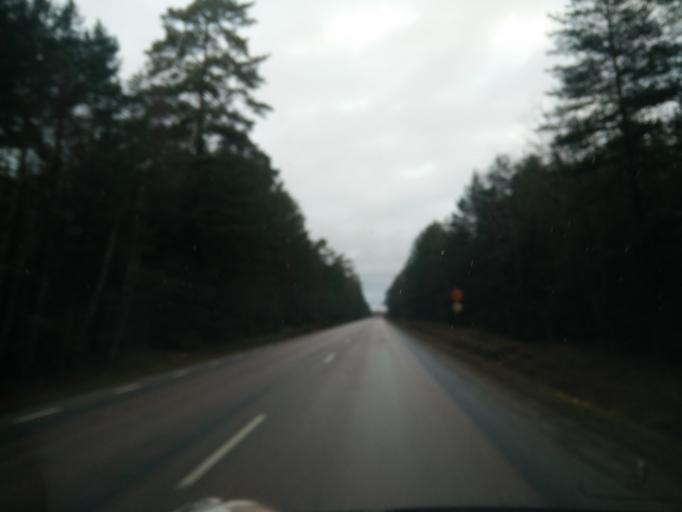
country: SE
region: Uppsala
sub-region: Enkopings Kommun
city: Enkoping
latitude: 59.6745
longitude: 17.0988
